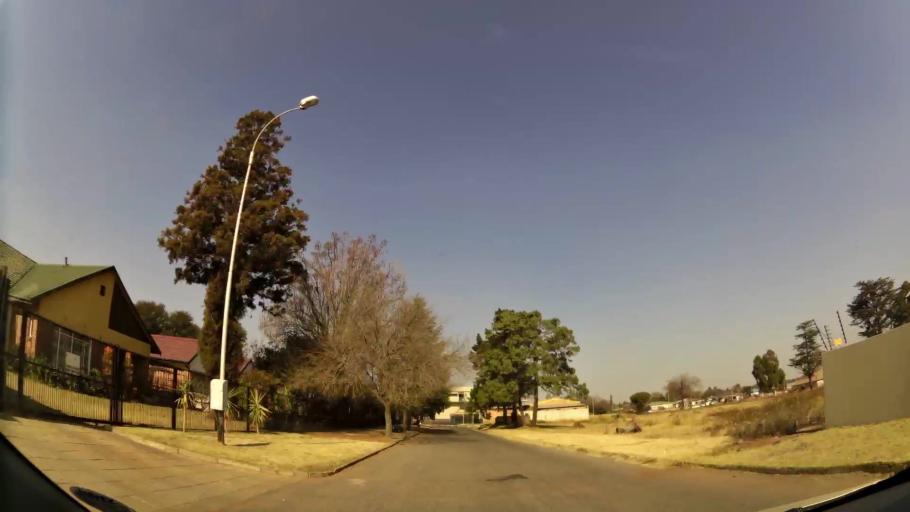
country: ZA
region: Gauteng
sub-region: West Rand District Municipality
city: Randfontein
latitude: -26.1667
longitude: 27.7032
